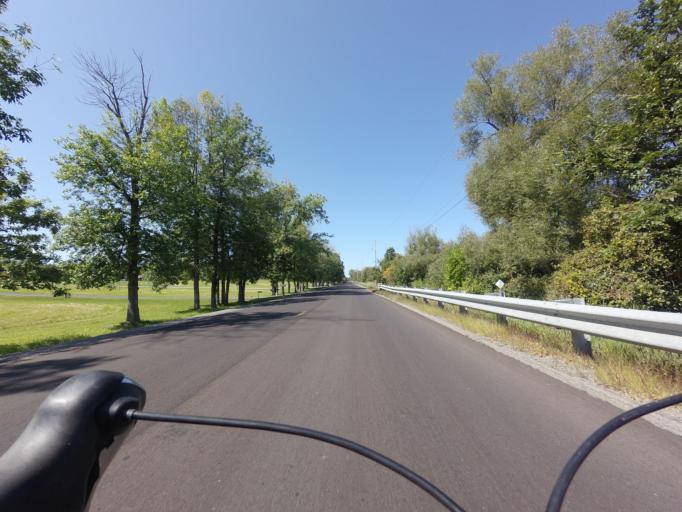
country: CA
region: Ontario
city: Bells Corners
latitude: 45.3741
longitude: -75.9332
